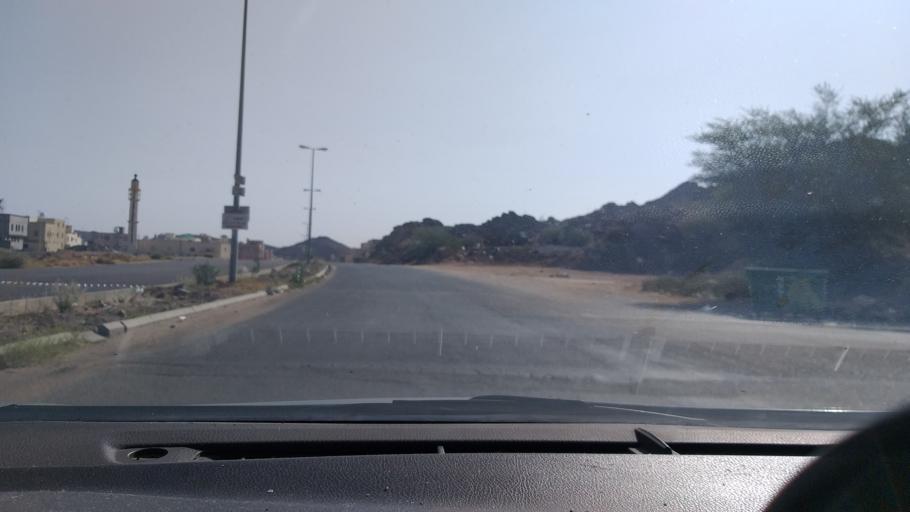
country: SA
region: Makkah
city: Ta'if
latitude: 21.2213
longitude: 40.3715
